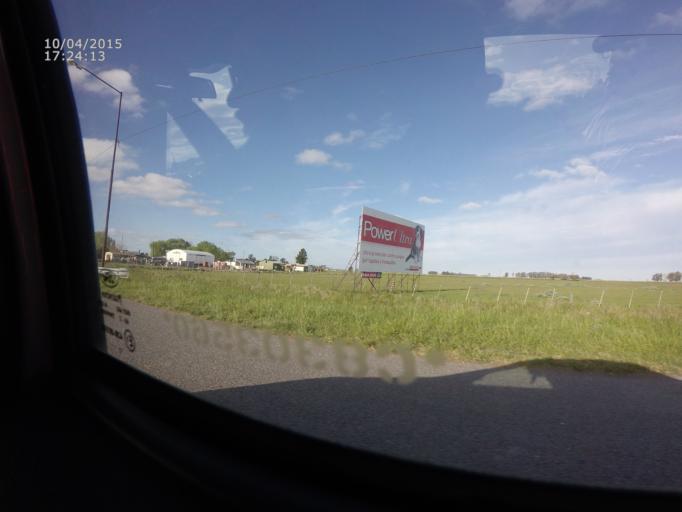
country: AR
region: Buenos Aires
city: Maipu
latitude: -37.0885
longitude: -57.8276
